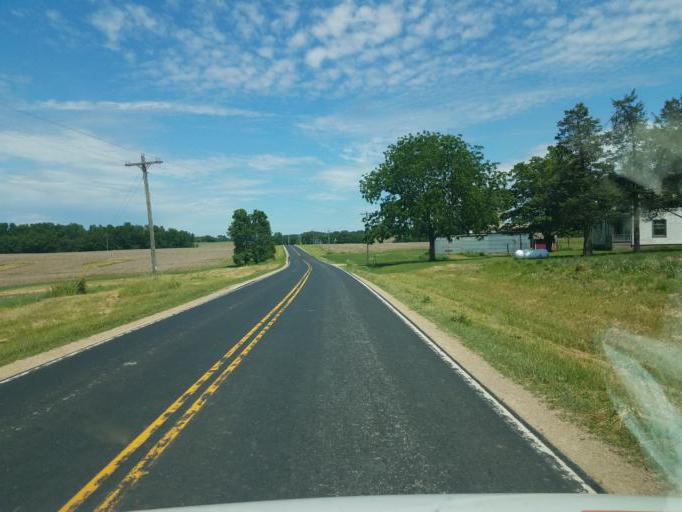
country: US
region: Wisconsin
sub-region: Vernon County
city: Hillsboro
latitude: 43.5918
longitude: -90.3296
